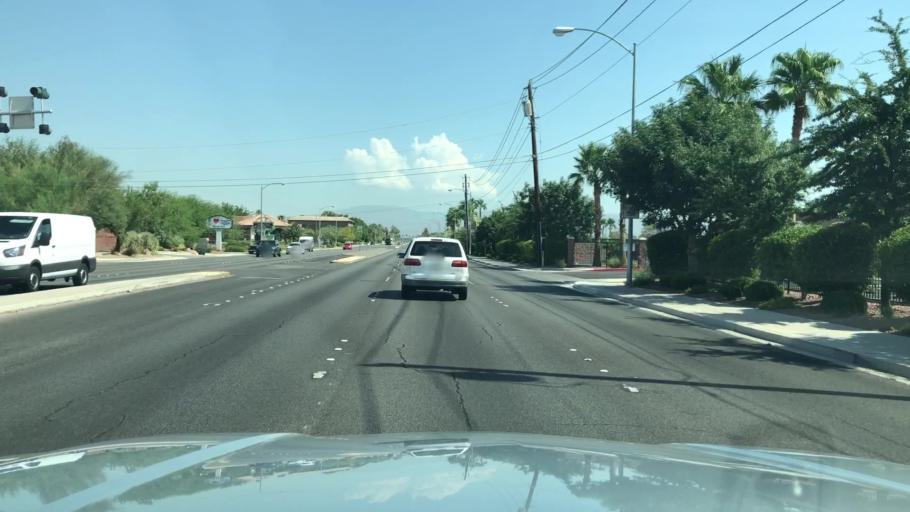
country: US
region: Nevada
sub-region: Clark County
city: Spring Valley
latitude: 36.1306
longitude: -115.2249
